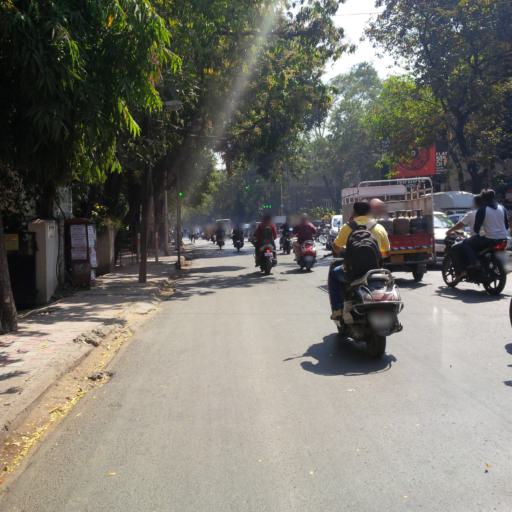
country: IN
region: Maharashtra
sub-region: Pune Division
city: Pune
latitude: 18.5113
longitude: 73.8292
